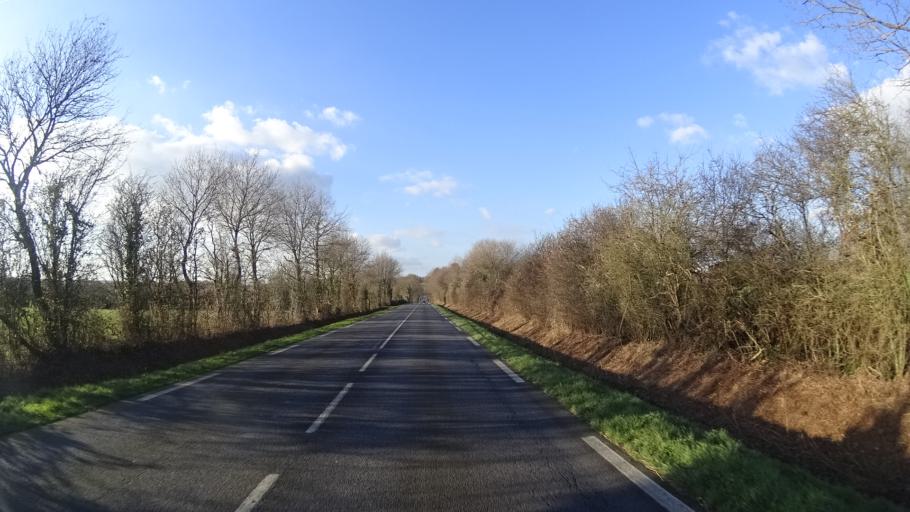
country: FR
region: Pays de la Loire
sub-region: Departement de la Loire-Atlantique
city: Guenrouet
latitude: 47.5413
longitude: -1.9347
